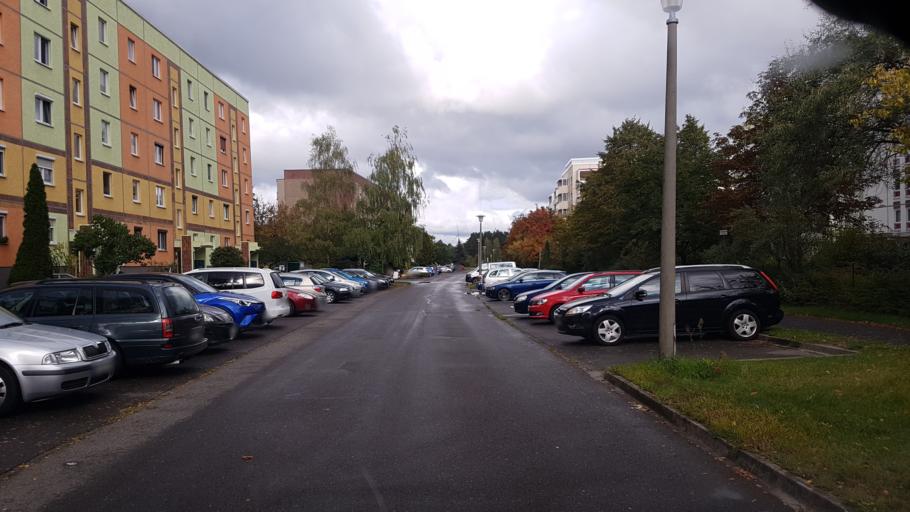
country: DE
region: Brandenburg
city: Grossraschen
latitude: 51.5964
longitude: 14.0009
